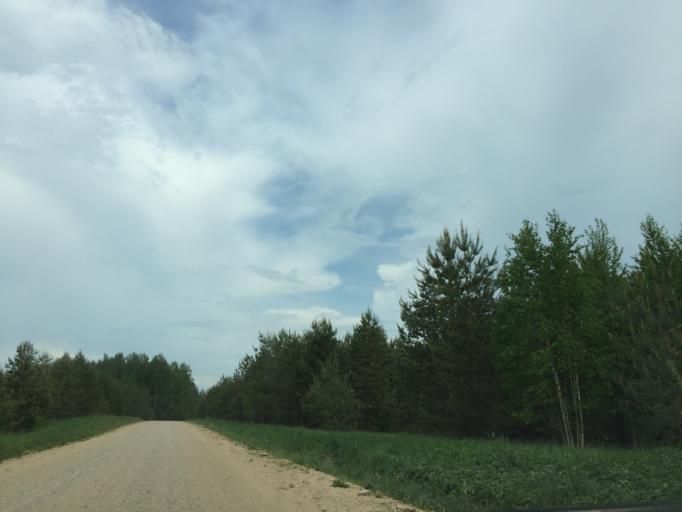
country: LV
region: Livani
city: Livani
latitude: 56.5677
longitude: 26.1481
